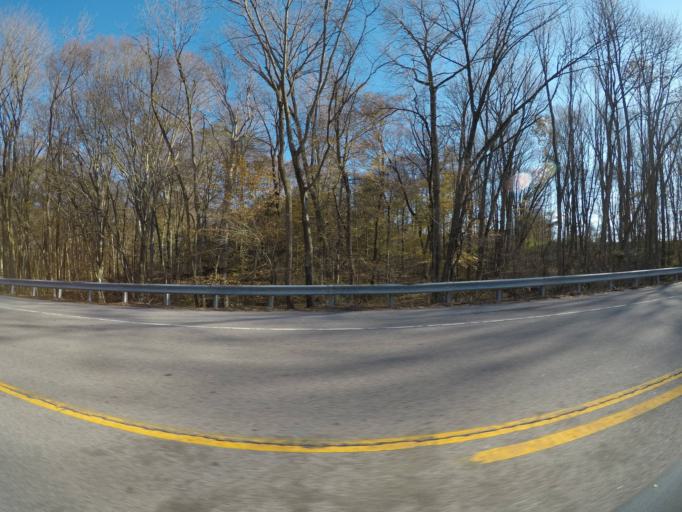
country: US
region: Maryland
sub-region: Cecil County
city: Rising Sun
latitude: 39.6990
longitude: -76.0873
